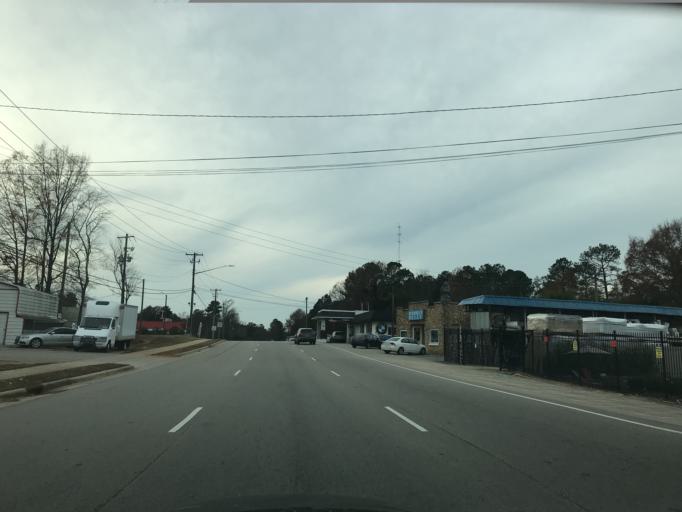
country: US
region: North Carolina
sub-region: Wake County
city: West Raleigh
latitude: 35.7864
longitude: -78.7209
